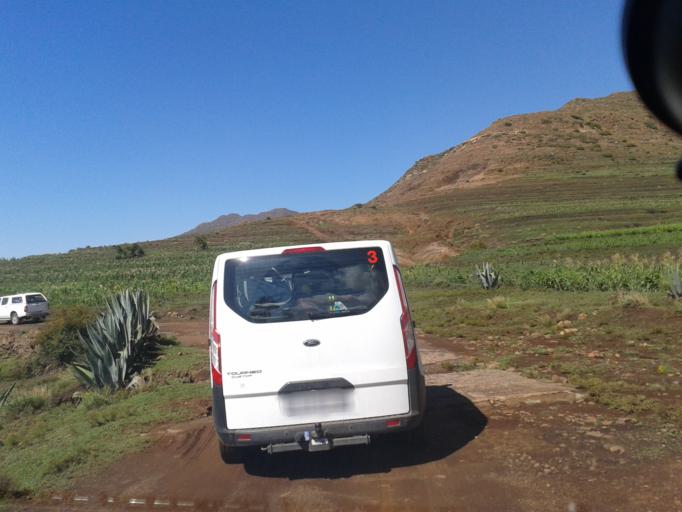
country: LS
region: Maseru
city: Nako
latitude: -29.8363
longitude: 27.5687
